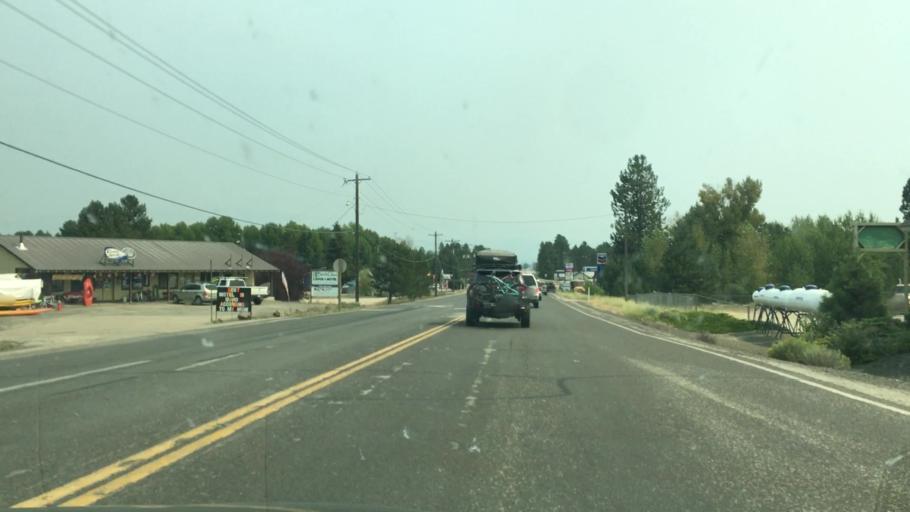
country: US
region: Idaho
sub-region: Valley County
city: Cascade
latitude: 44.5065
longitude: -116.0314
